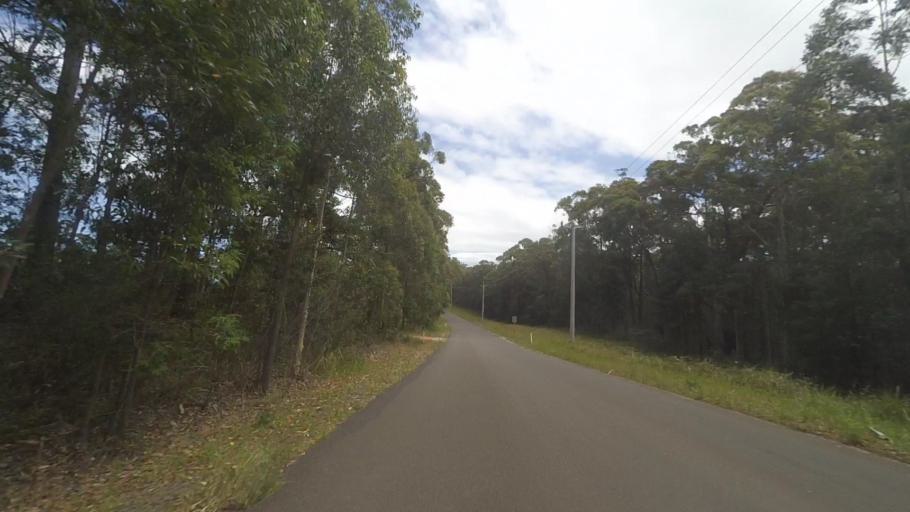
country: AU
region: New South Wales
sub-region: Shoalhaven Shire
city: Milton
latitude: -35.3790
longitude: 150.3738
